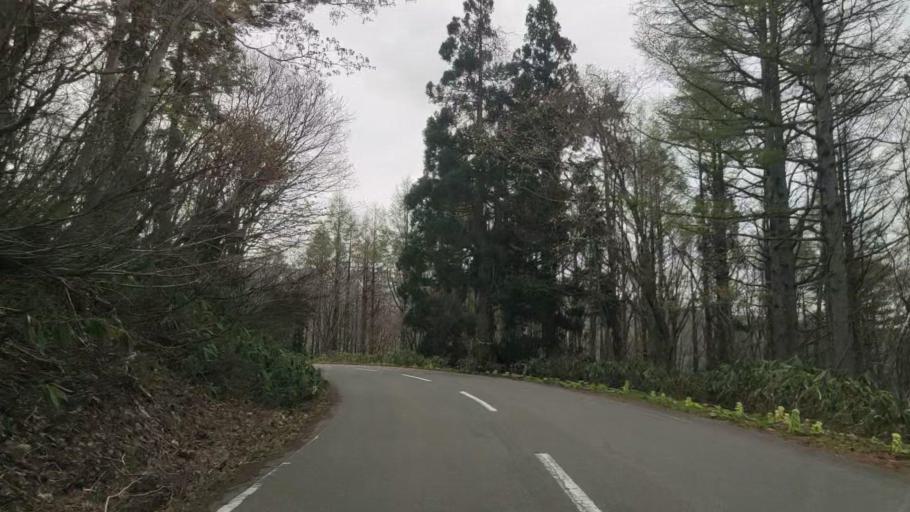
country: JP
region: Aomori
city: Aomori Shi
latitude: 40.7186
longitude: 140.8623
